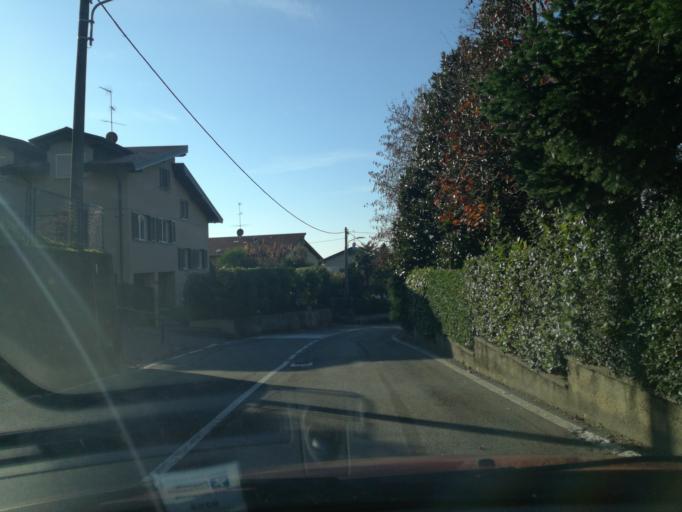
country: IT
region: Lombardy
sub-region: Provincia di Lecco
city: Robbiate
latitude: 45.6997
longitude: 9.4321
